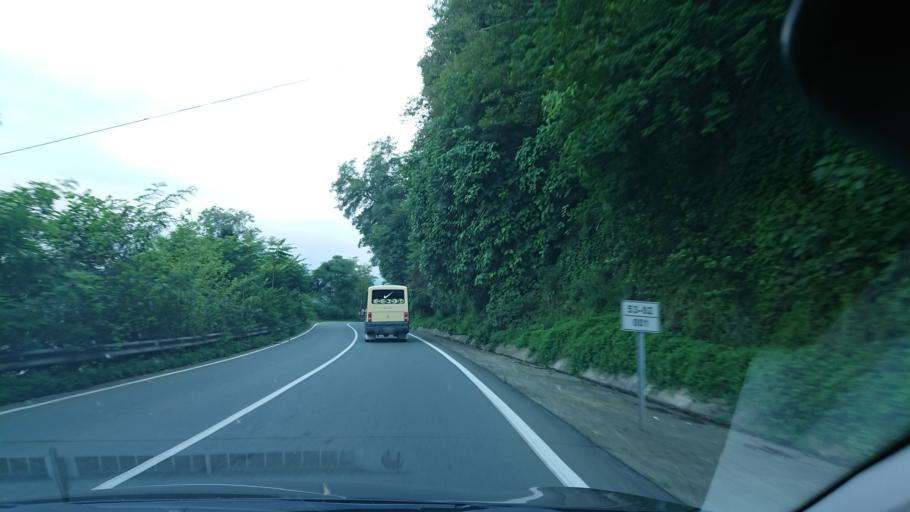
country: TR
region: Rize
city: Cayeli
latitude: 41.0752
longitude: 40.7112
